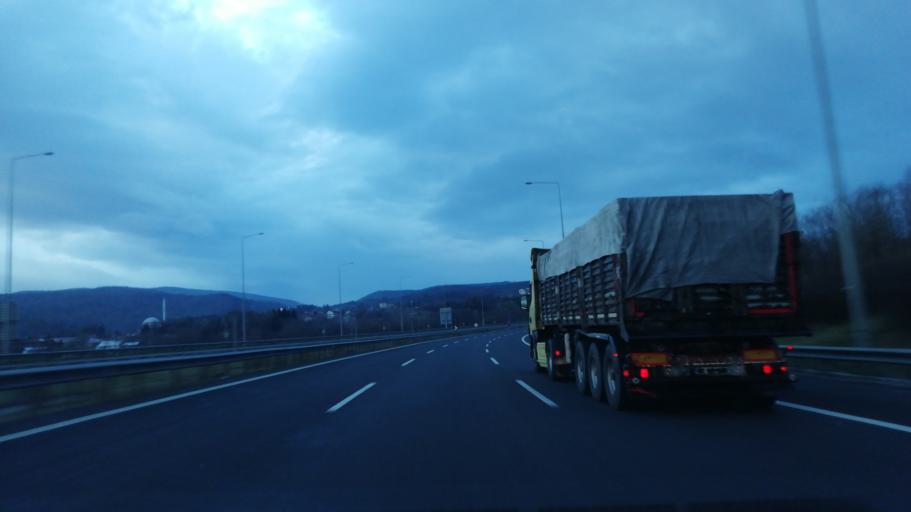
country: TR
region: Duzce
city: Kaynasli
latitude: 40.7241
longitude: 31.4508
